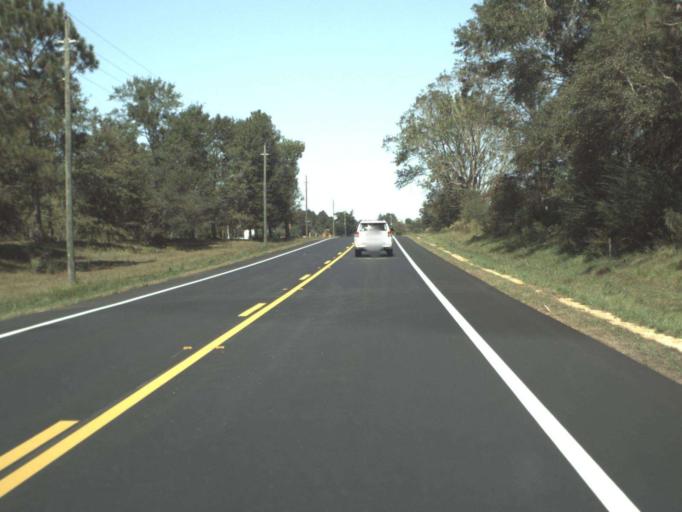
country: US
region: Alabama
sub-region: Covington County
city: Florala
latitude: 30.9396
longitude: -86.2824
